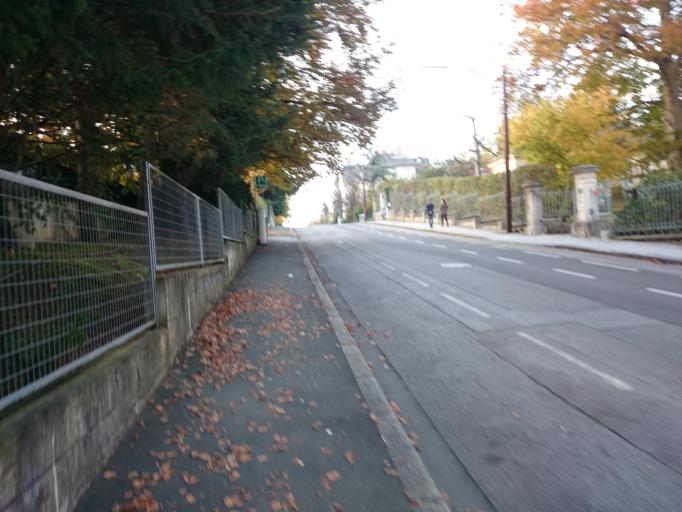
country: AT
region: Styria
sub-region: Graz Stadt
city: Graz
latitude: 47.0800
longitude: 15.4552
